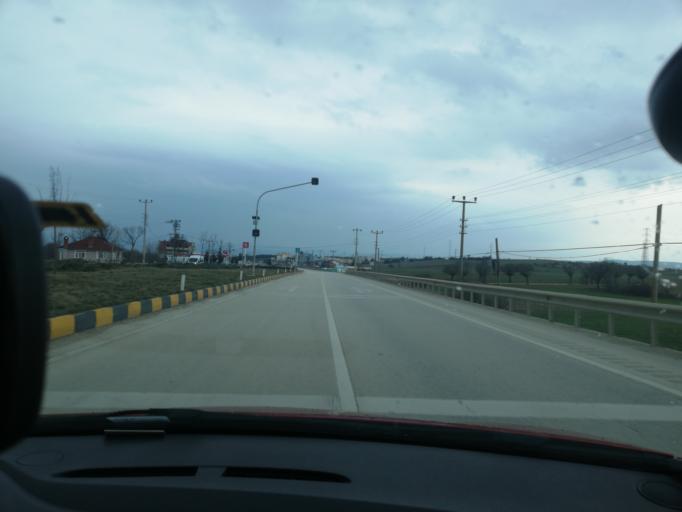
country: TR
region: Kastamonu
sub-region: Cide
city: Kastamonu
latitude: 41.4815
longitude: 33.7661
